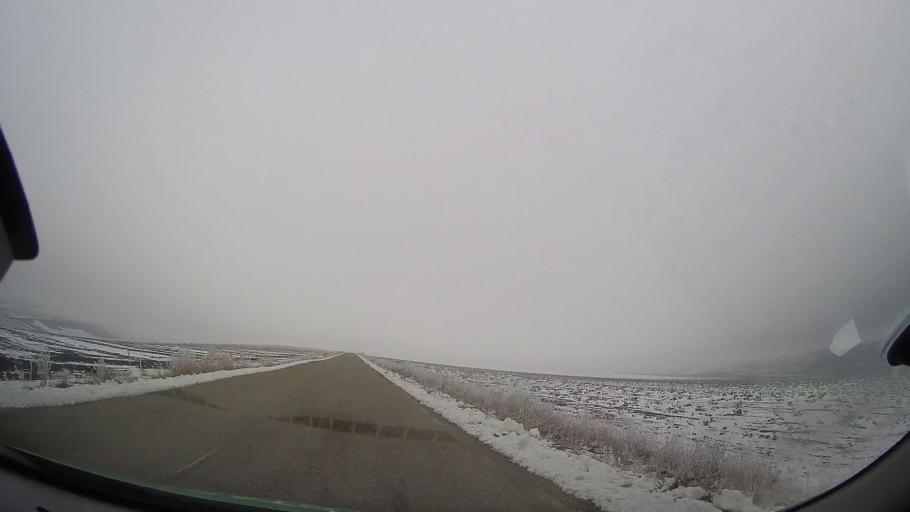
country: RO
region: Vaslui
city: Coroiesti
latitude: 46.2132
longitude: 27.4814
